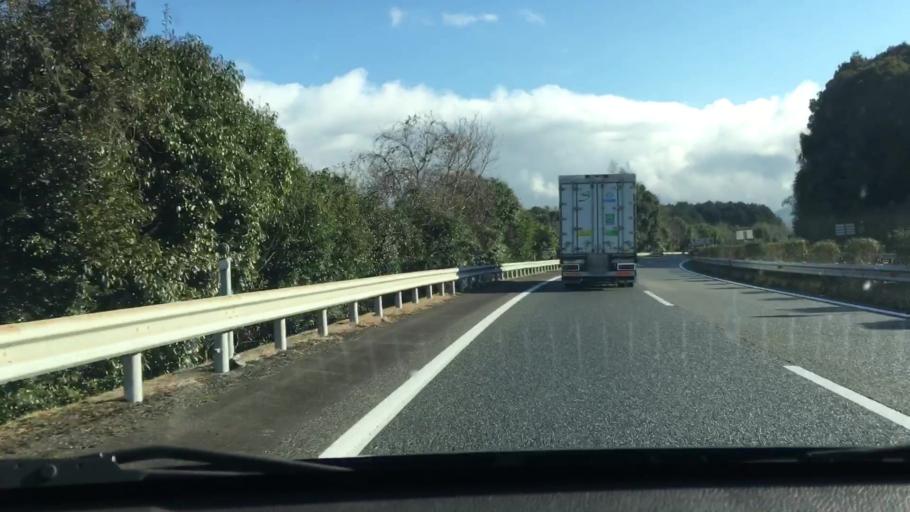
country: JP
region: Kumamoto
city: Hitoyoshi
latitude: 32.1695
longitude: 130.7924
